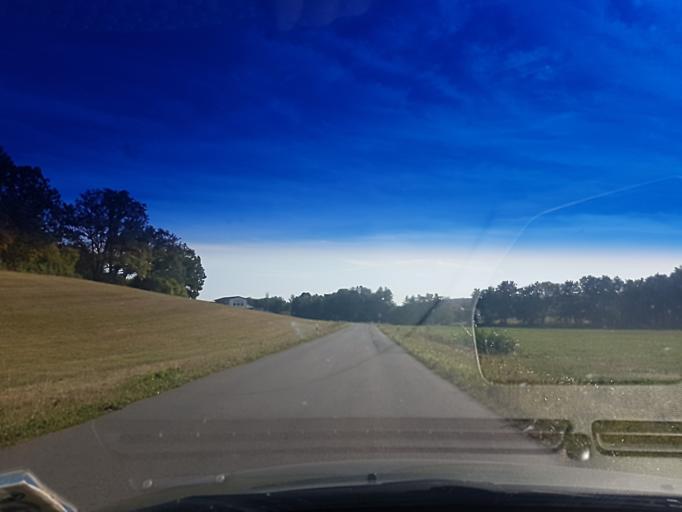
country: DE
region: Bavaria
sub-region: Upper Franconia
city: Schlusselfeld
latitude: 49.7669
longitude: 10.6127
